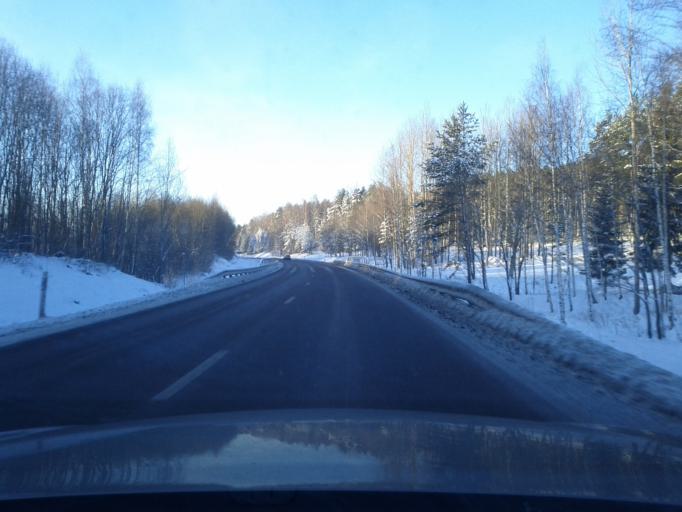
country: SE
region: Dalarna
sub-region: Faluns Kommun
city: Falun
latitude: 60.6232
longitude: 15.6430
